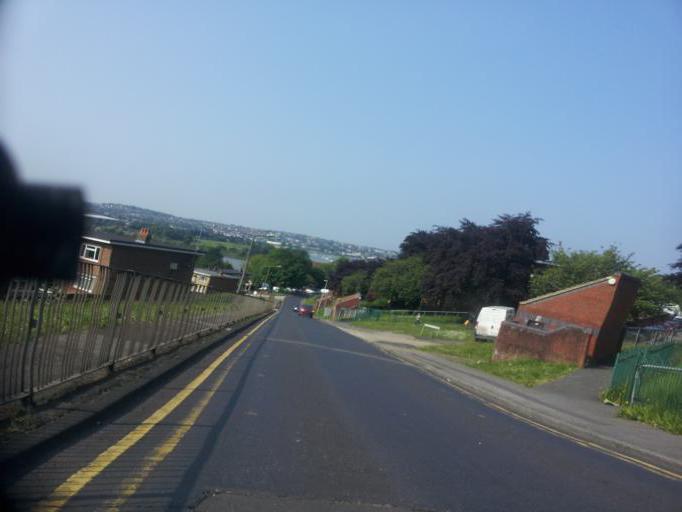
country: GB
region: England
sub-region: Medway
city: Rochester
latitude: 51.3751
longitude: 0.4884
